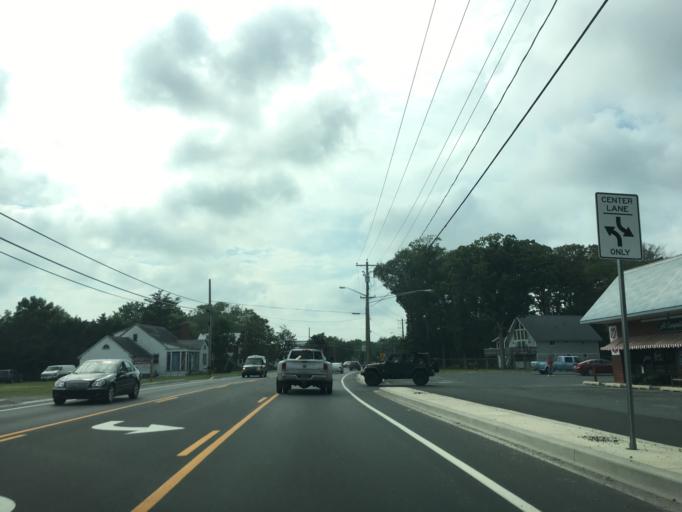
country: US
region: Delaware
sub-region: Sussex County
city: Ocean View
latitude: 38.5487
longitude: -75.1203
